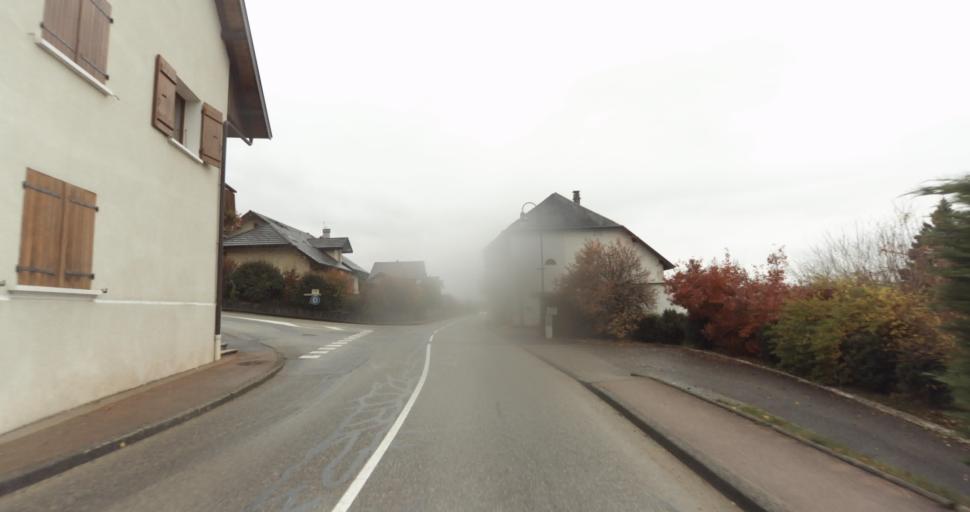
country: FR
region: Rhone-Alpes
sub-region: Departement de la Haute-Savoie
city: Viuz-la-Chiesaz
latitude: 45.8091
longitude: 6.0619
